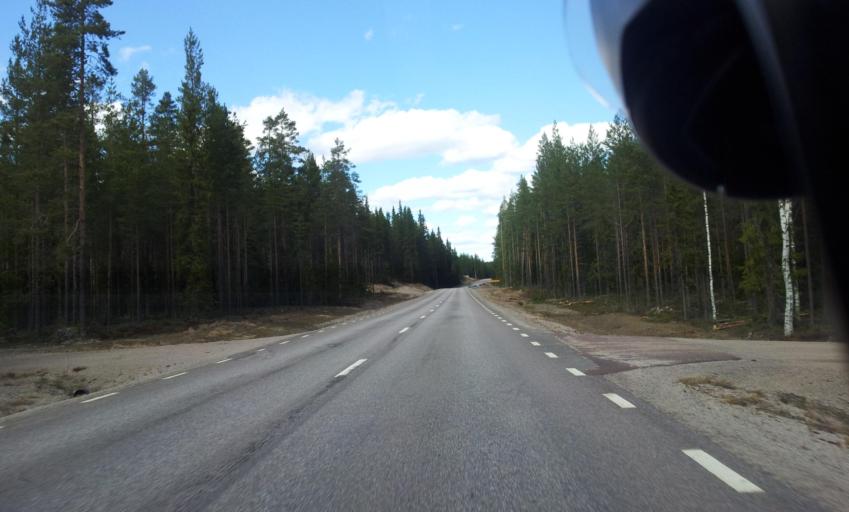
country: SE
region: Gaevleborg
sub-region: Ovanakers Kommun
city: Edsbyn
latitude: 61.1646
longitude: 15.8823
